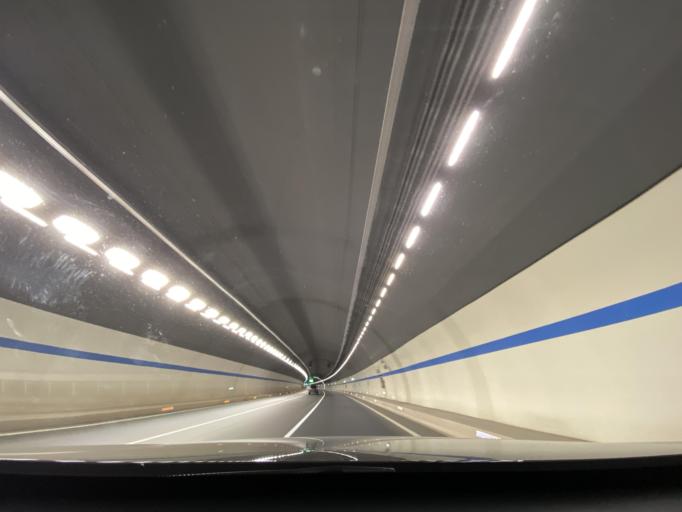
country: CN
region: Sichuan
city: Longquan
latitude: 30.4434
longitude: 104.2430
